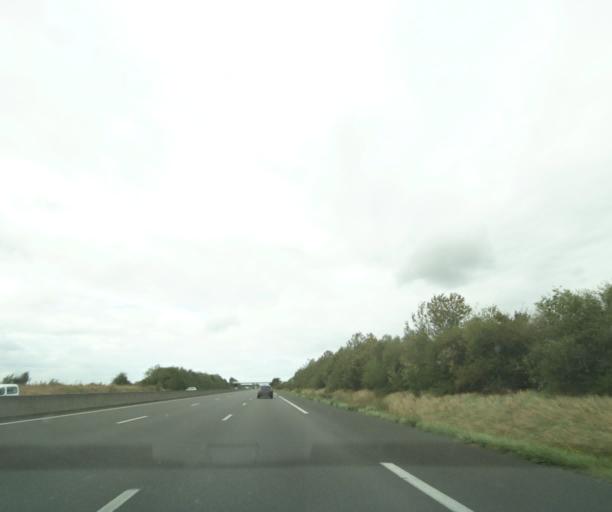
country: FR
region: Ile-de-France
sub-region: Departement de l'Essonne
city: Corbreuse
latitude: 48.4776
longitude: 1.9132
